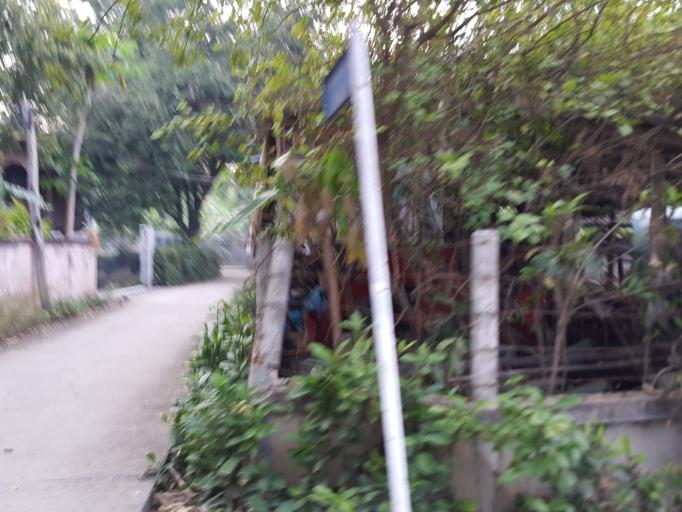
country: TH
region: Chiang Mai
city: San Sai
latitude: 18.8921
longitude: 99.1294
